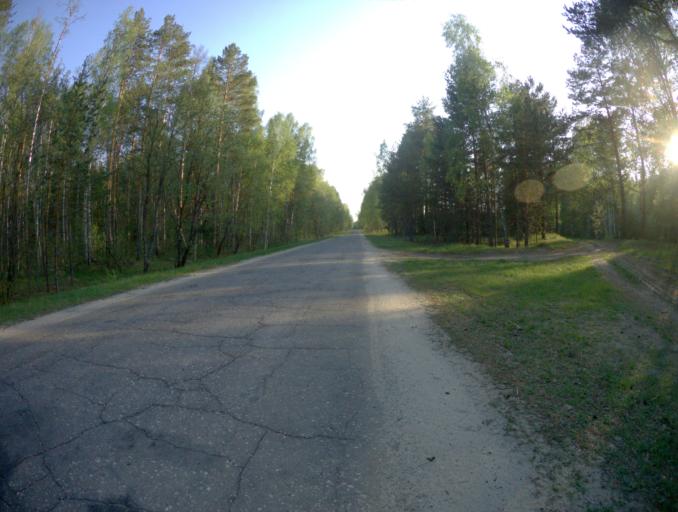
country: RU
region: Vladimir
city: Vyazniki
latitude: 56.3354
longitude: 42.1313
